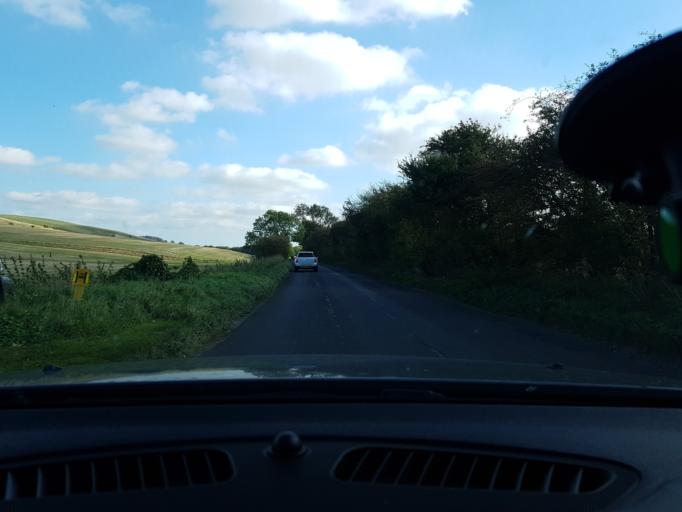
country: GB
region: England
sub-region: Borough of Swindon
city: Bishopstone
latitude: 51.5210
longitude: -1.6565
